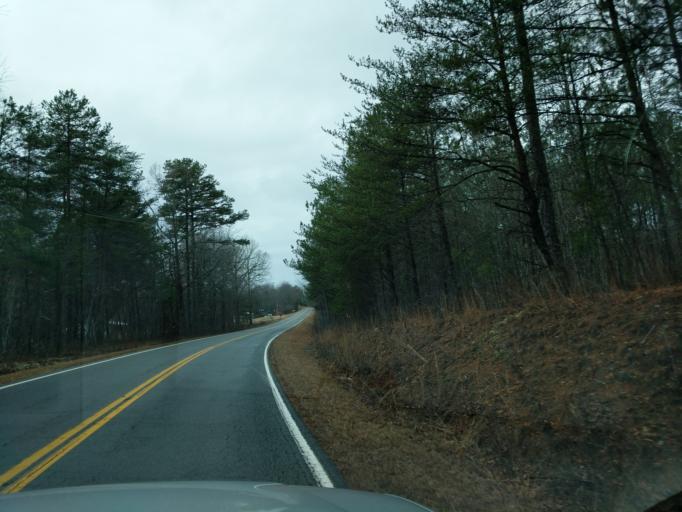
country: US
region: South Carolina
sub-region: Oconee County
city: Walhalla
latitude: 34.7940
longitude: -83.1659
